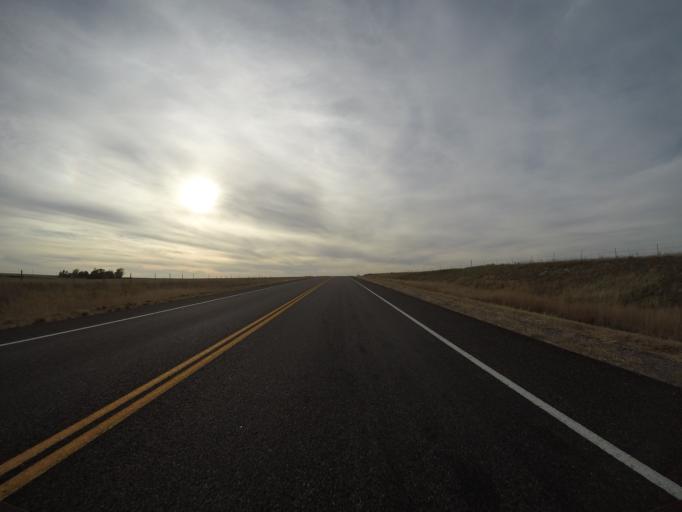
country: US
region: Kansas
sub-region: Cheyenne County
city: Saint Francis
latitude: 39.7466
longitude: -102.0864
